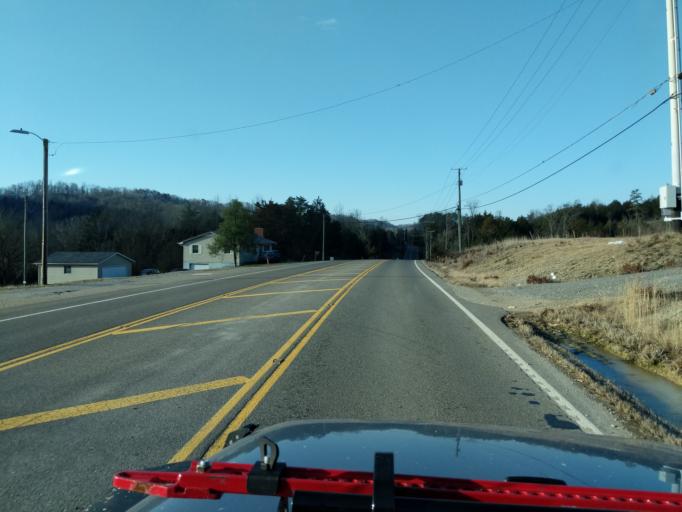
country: US
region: Tennessee
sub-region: Anderson County
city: Norris
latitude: 36.1037
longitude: -84.0274
